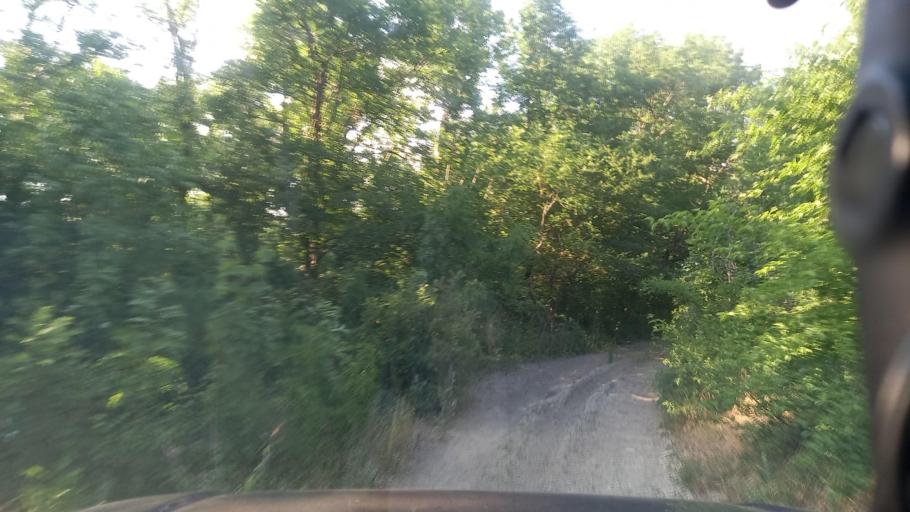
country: RU
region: Krasnodarskiy
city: Divnomorskoye
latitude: 44.5933
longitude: 38.2792
